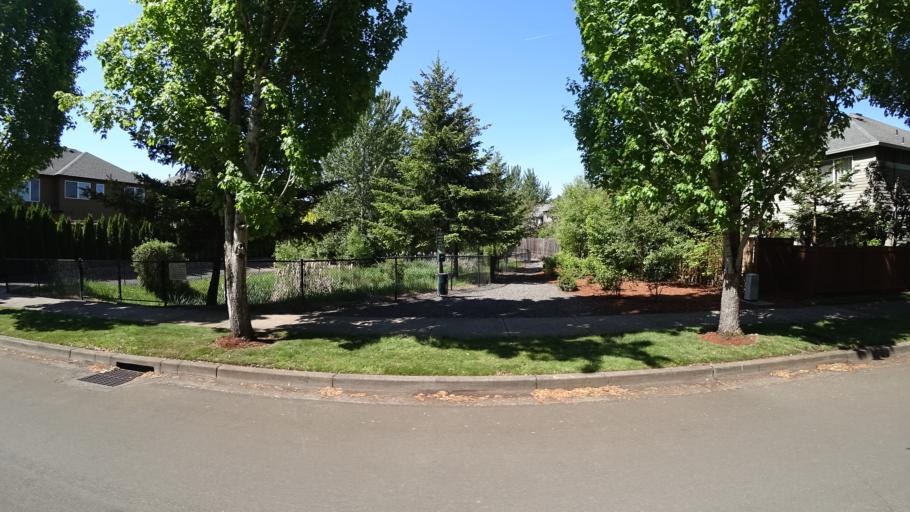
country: US
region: Oregon
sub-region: Washington County
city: Rockcreek
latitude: 45.5277
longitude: -122.9203
